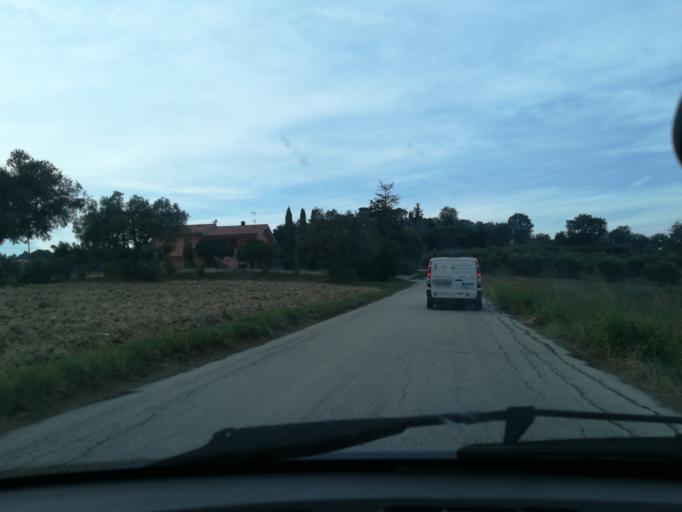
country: IT
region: The Marches
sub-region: Provincia di Macerata
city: Piediripa
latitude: 43.2930
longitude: 13.4879
